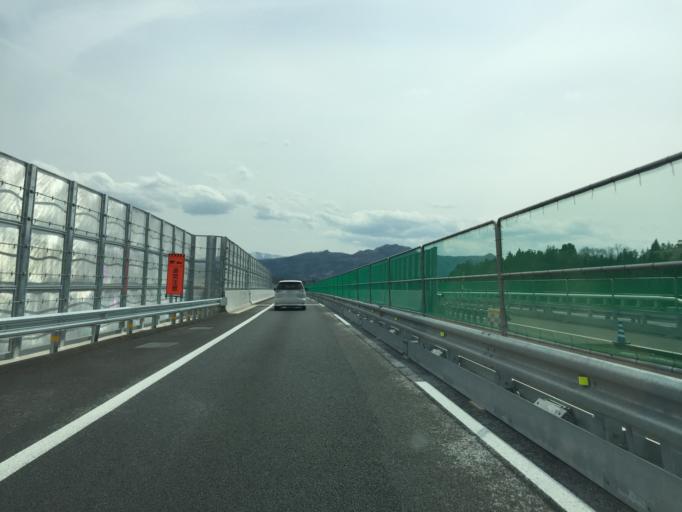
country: JP
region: Yamagata
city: Kaminoyama
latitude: 38.1938
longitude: 140.2992
